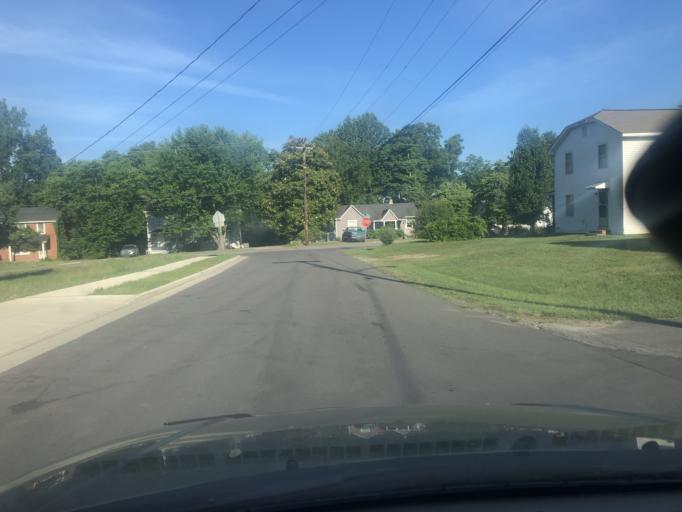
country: US
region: Tennessee
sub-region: Davidson County
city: Lakewood
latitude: 36.2598
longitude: -86.6541
